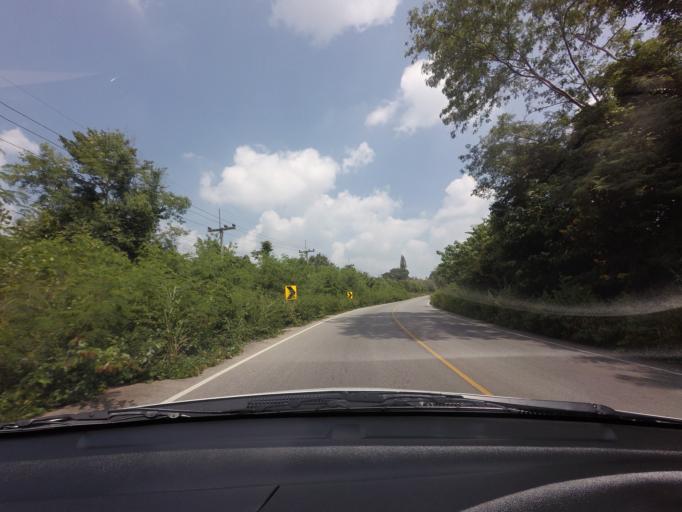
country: TH
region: Nakhon Ratchasima
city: Pak Chong
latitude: 14.6011
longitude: 101.5711
